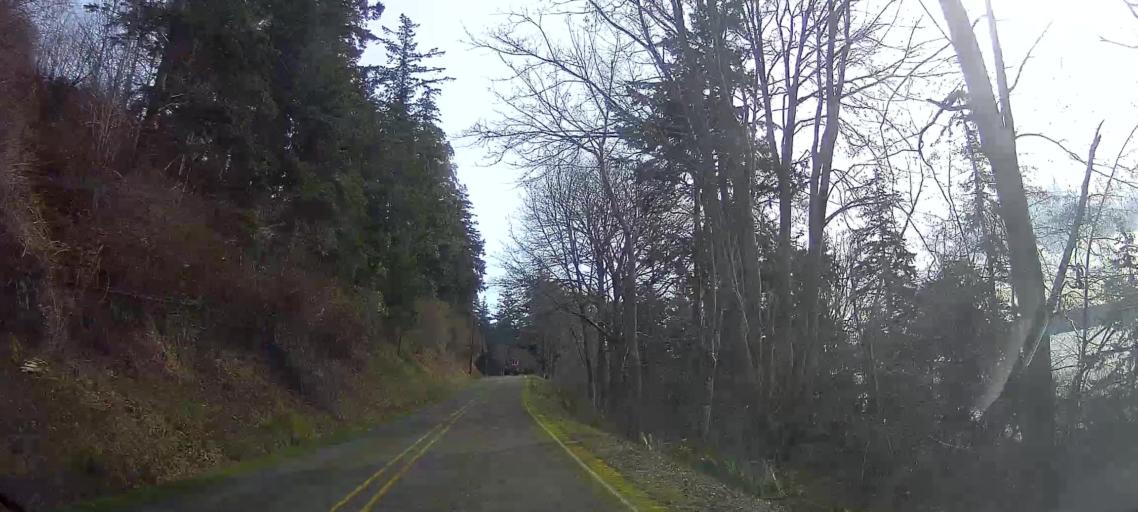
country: US
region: Washington
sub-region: Island County
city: Langley
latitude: 48.0659
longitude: -122.3862
